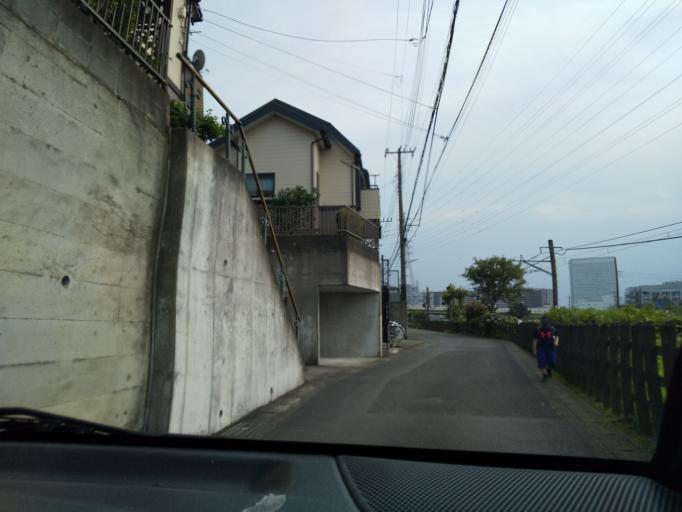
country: JP
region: Kanagawa
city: Zama
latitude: 35.4656
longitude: 139.3949
